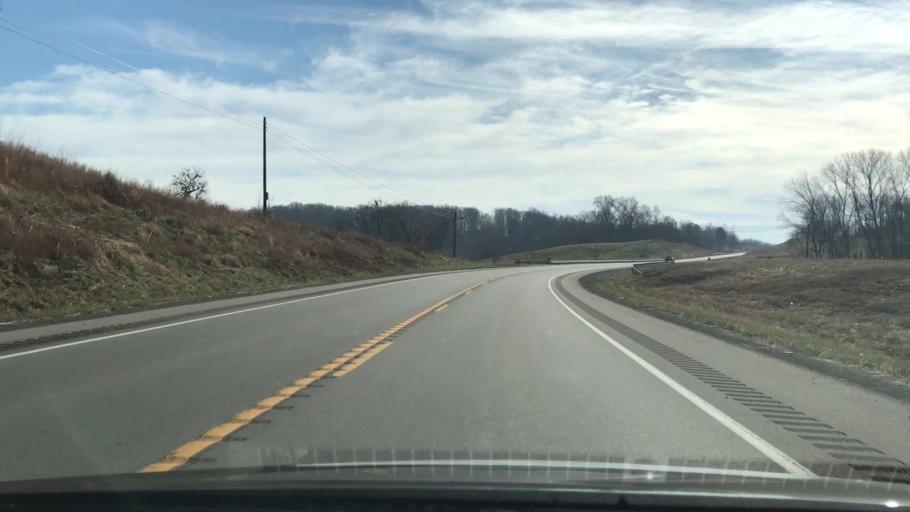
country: US
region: Kentucky
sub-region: Monroe County
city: Tompkinsville
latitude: 36.7800
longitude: -85.6849
